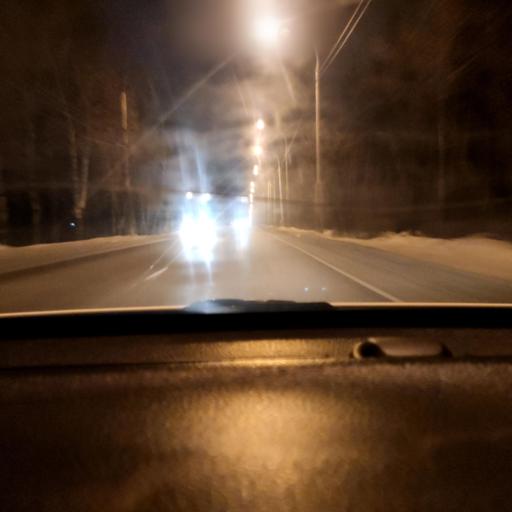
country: RU
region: Voronezj
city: Somovo
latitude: 51.7068
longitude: 39.2914
